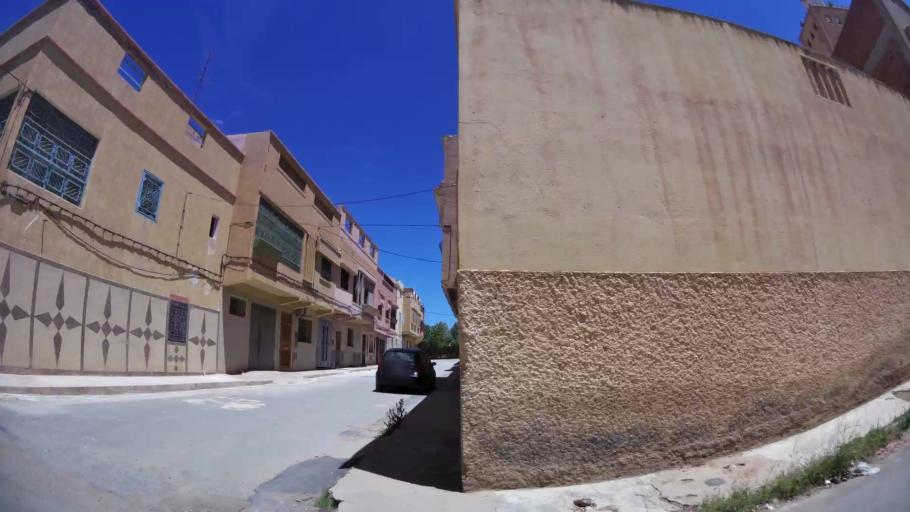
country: MA
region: Oriental
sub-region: Oujda-Angad
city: Oujda
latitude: 34.6673
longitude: -1.9244
